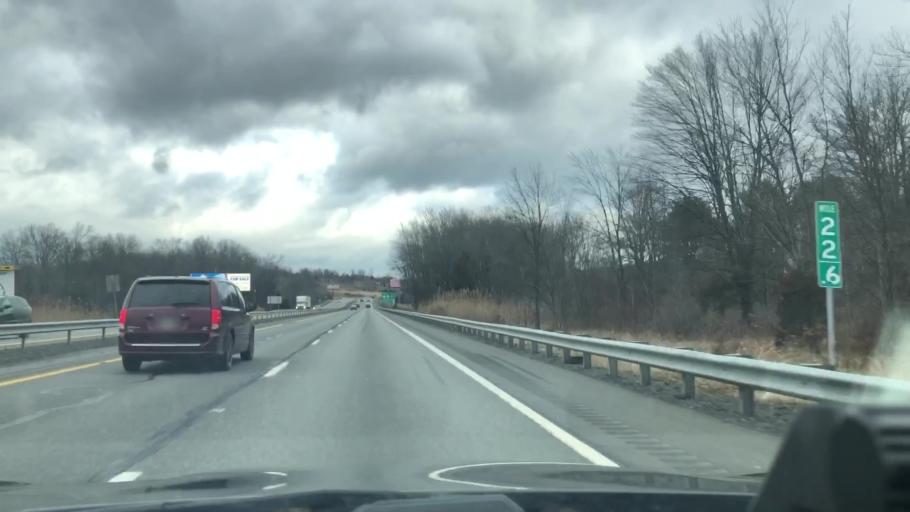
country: US
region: Pennsylvania
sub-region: Monroe County
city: Saylorsburg
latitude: 40.9193
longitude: -75.2993
